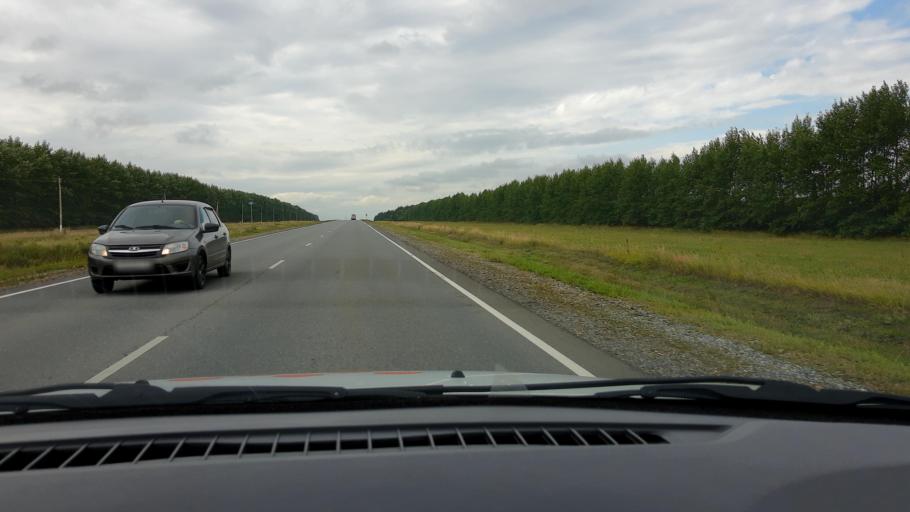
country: RU
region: Tatarstan
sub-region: Alekseyevskiy Rayon
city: Alekseyevskoye
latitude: 55.3106
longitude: 50.3608
